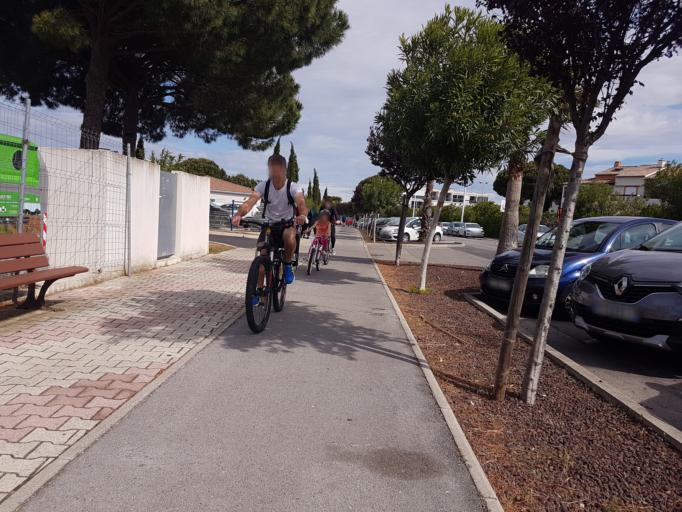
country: FR
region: Languedoc-Roussillon
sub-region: Departement du Gard
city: Le Grau-du-Roi
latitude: 43.5483
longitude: 4.1229
